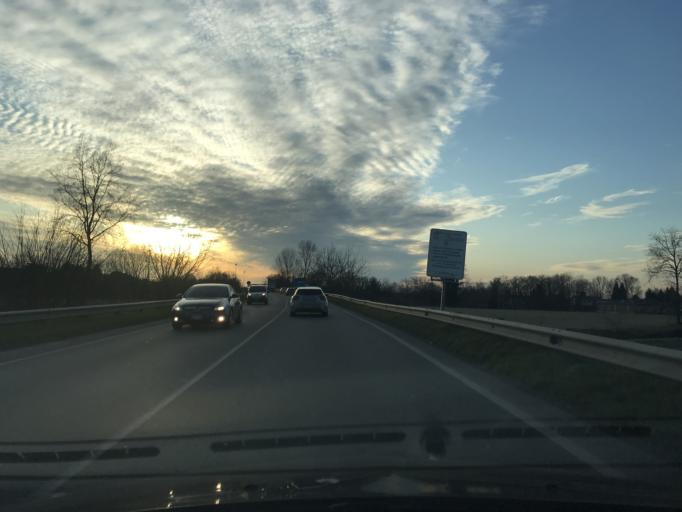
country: IT
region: Lombardy
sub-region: Provincia di Lodi
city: Castiraga Vidardo
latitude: 45.2482
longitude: 9.4066
